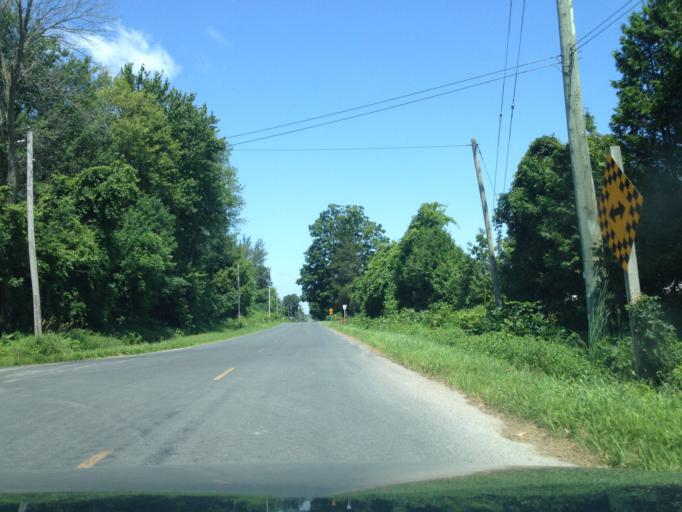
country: CA
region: Ontario
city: Aylmer
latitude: 42.6378
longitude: -80.7206
